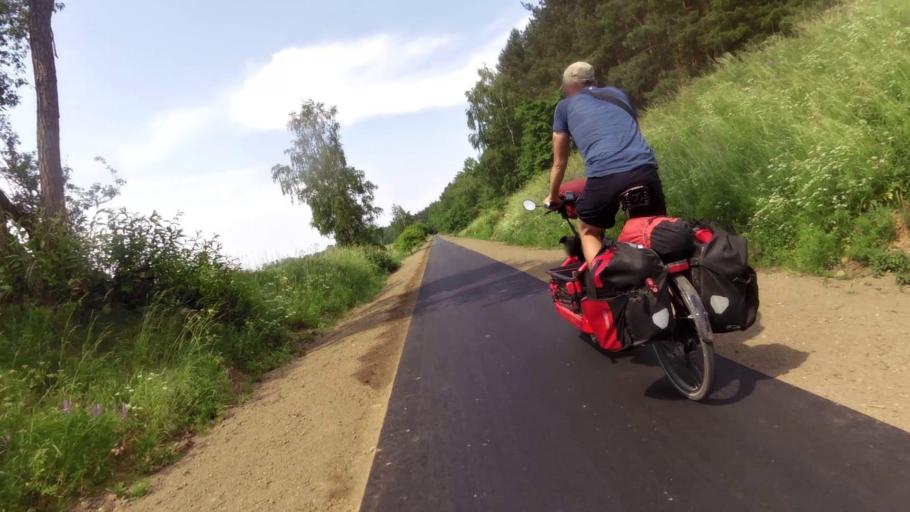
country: PL
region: West Pomeranian Voivodeship
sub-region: Powiat gryfinski
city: Banie
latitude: 53.1995
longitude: 14.6182
